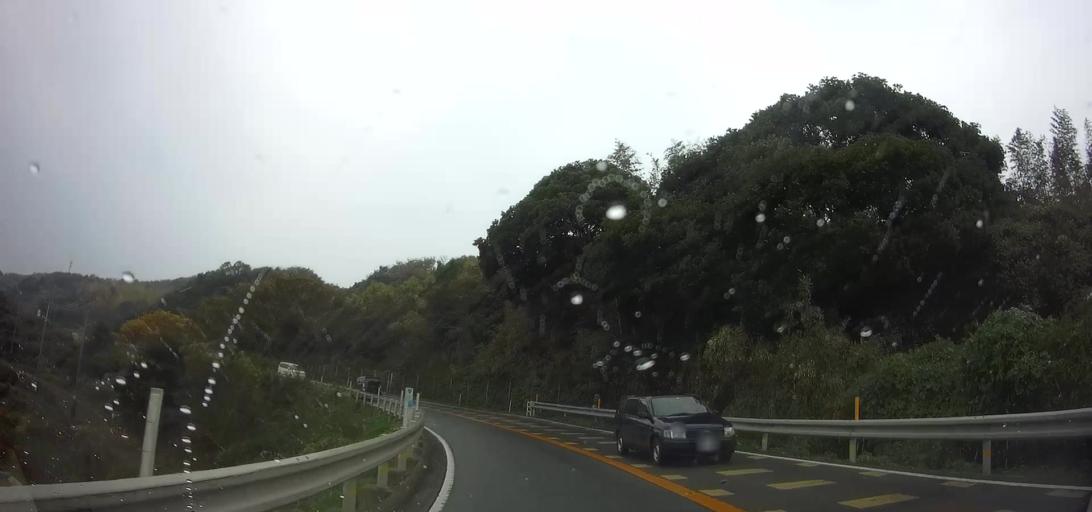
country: JP
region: Nagasaki
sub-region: Isahaya-shi
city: Isahaya
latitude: 32.7942
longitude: 130.1832
